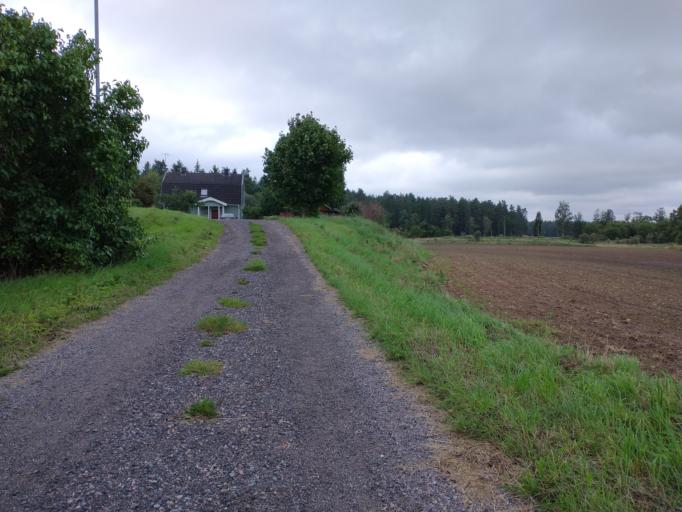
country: SE
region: Kalmar
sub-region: Kalmar Kommun
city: Lindsdal
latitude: 56.7795
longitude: 16.2967
